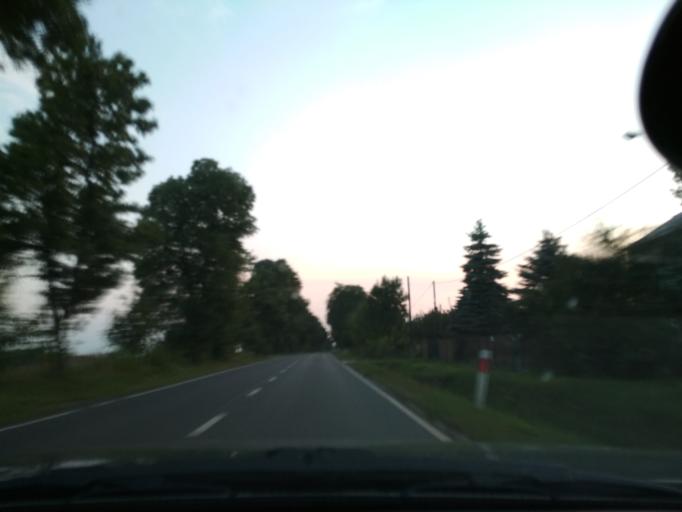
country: PL
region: Silesian Voivodeship
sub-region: Powiat zawiercianski
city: Pilica
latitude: 50.4682
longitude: 19.6205
